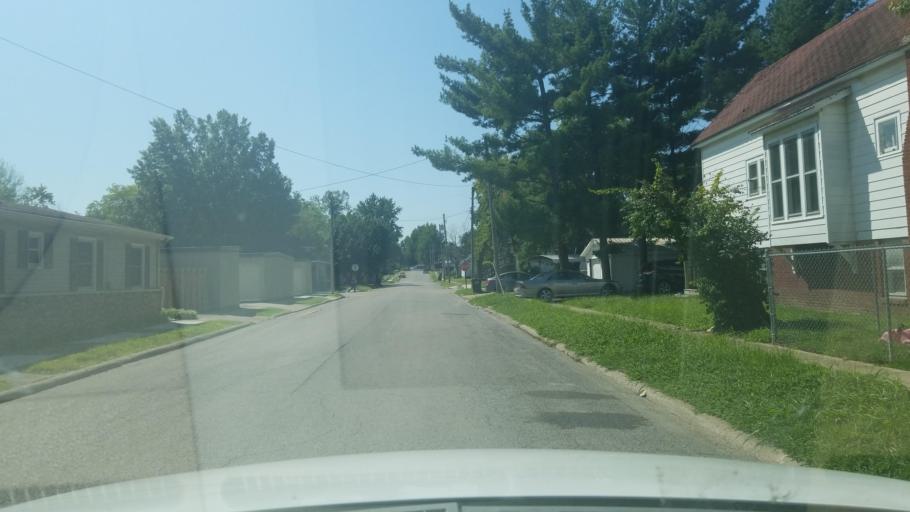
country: US
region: Illinois
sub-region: Saline County
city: Harrisburg
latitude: 37.7318
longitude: -88.5436
